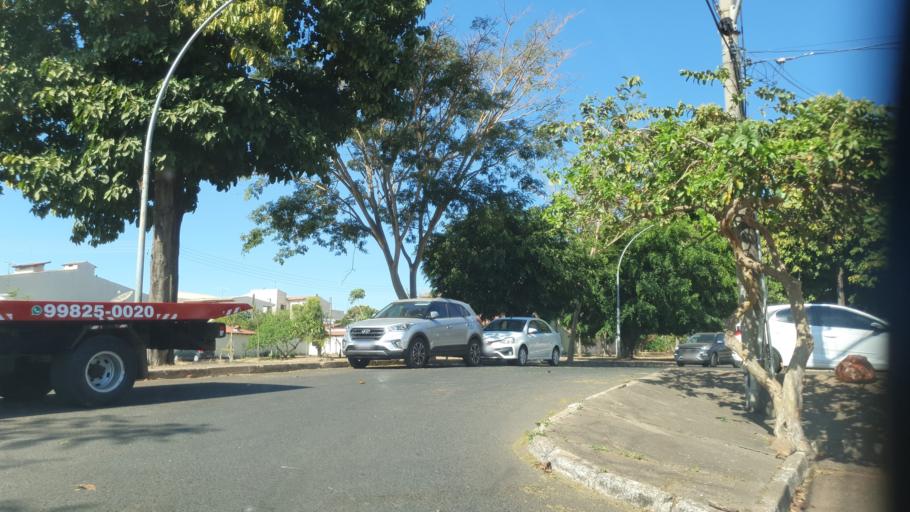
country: BR
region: Federal District
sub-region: Brasilia
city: Brasilia
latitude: -15.7894
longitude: -47.9351
